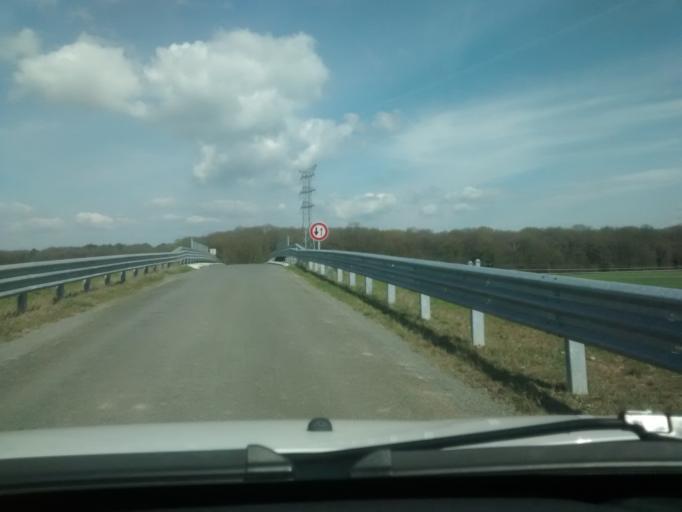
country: FR
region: Brittany
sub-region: Departement d'Ille-et-Vilaine
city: Chateaugiron
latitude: 48.0704
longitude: -1.5004
